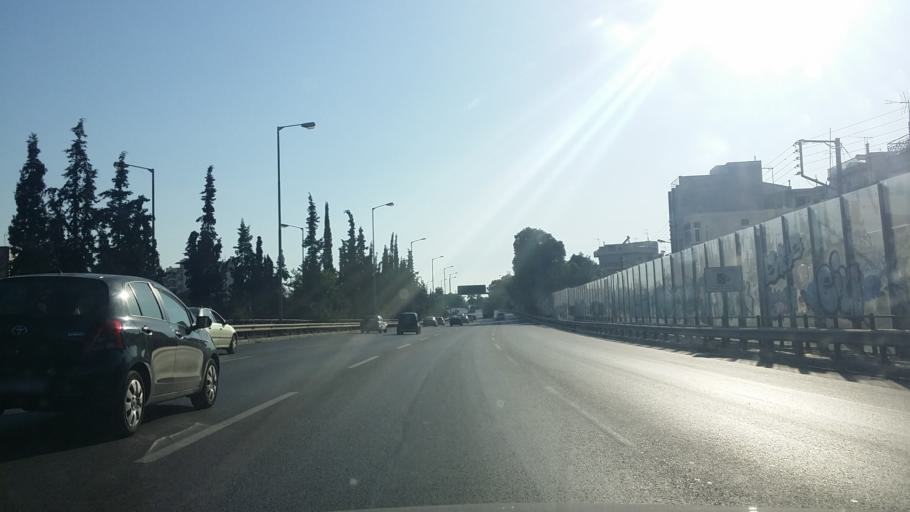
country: GR
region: Attica
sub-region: Nomarchia Athinas
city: Agioi Anargyroi
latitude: 38.0187
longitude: 23.7225
